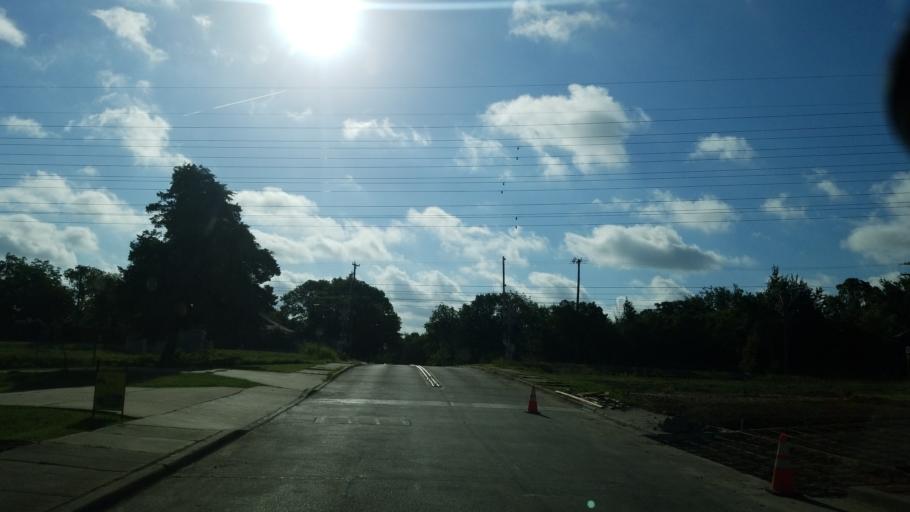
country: US
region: Texas
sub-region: Dallas County
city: Dallas
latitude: 32.7296
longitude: -96.8048
